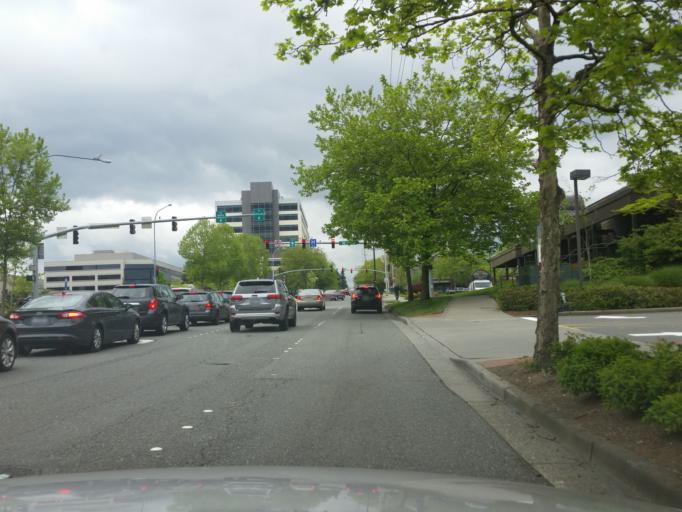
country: US
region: Washington
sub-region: King County
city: Bellevue
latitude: 47.6186
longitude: -122.1856
